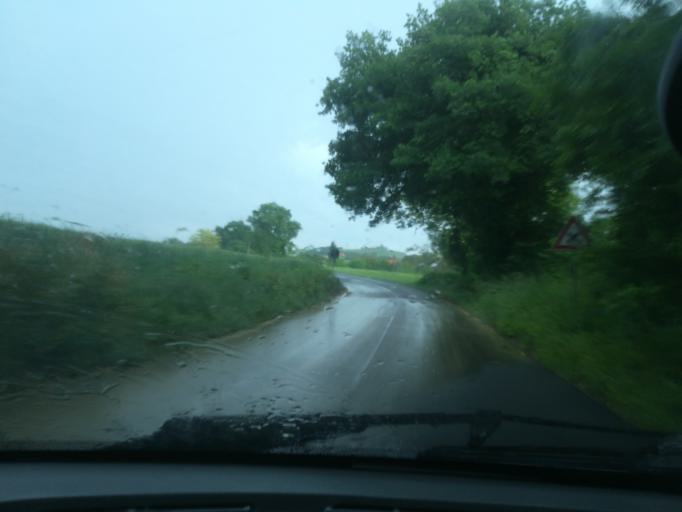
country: IT
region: The Marches
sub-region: Provincia di Macerata
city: Passo di Treia
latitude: 43.3103
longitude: 13.3418
